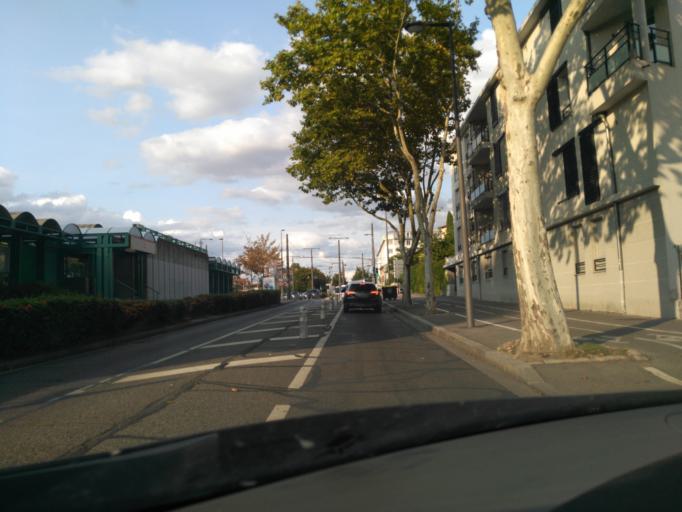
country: FR
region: Rhone-Alpes
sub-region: Departement du Rhone
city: Caluire-et-Cuire
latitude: 45.7850
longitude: 4.8325
